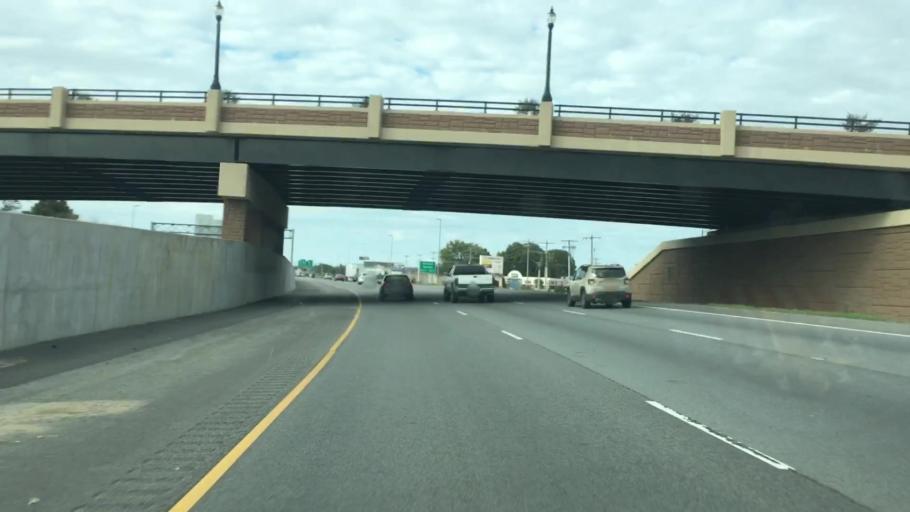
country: US
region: Arkansas
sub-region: Faulkner County
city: Conway
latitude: 35.0841
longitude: -92.4150
